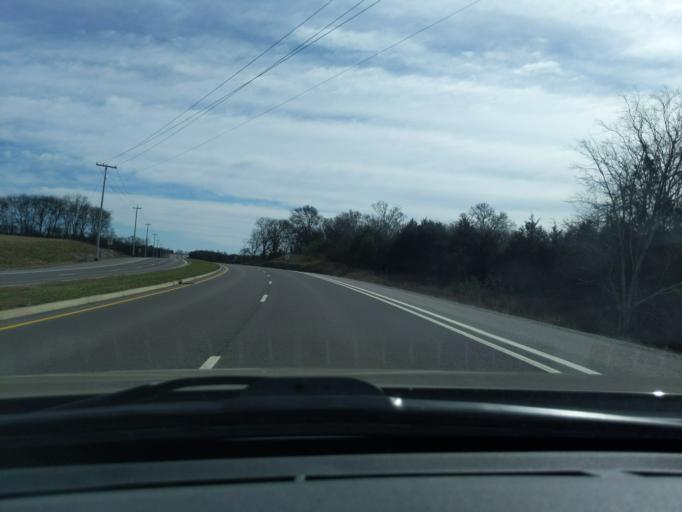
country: US
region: Tennessee
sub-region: Wilson County
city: Mount Juliet
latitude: 36.2003
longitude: -86.4952
